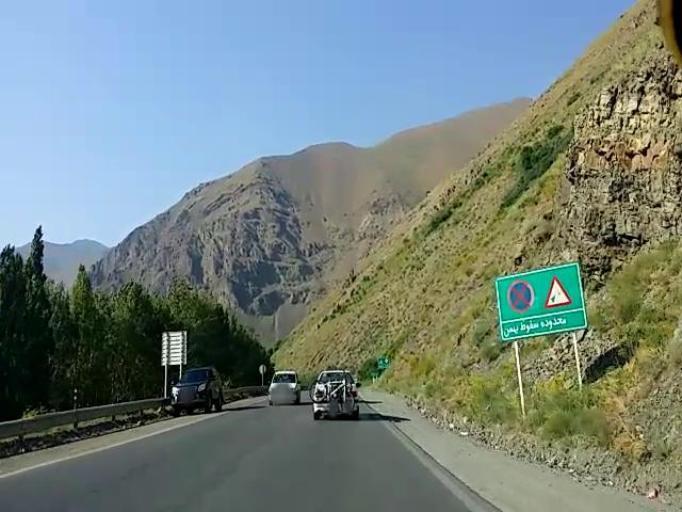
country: IR
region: Tehran
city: Tajrish
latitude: 36.1071
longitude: 51.3184
